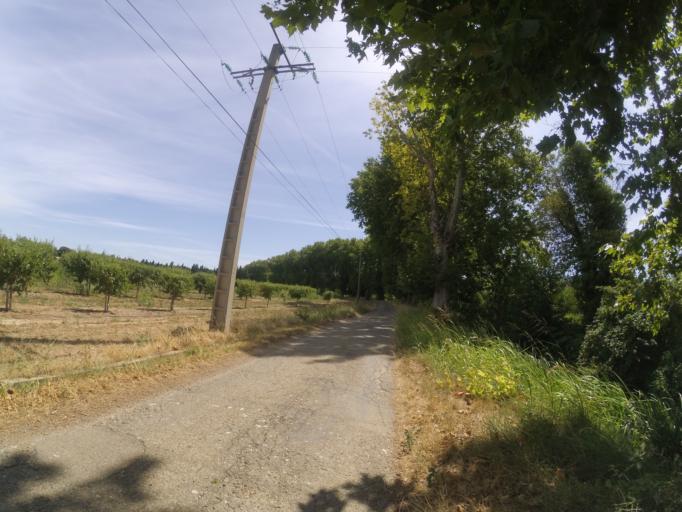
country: FR
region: Languedoc-Roussillon
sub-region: Departement des Pyrenees-Orientales
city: Ille-sur-Tet
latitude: 42.6733
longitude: 2.6522
